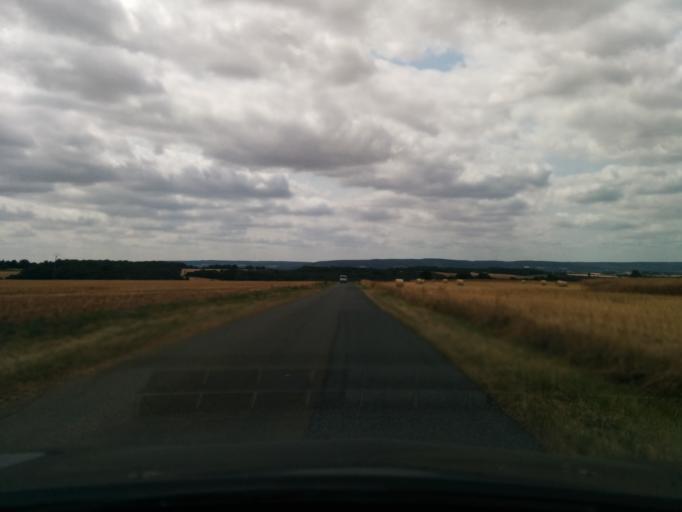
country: FR
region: Centre
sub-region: Departement du Cher
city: Sancerre
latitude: 47.3259
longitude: 2.7760
